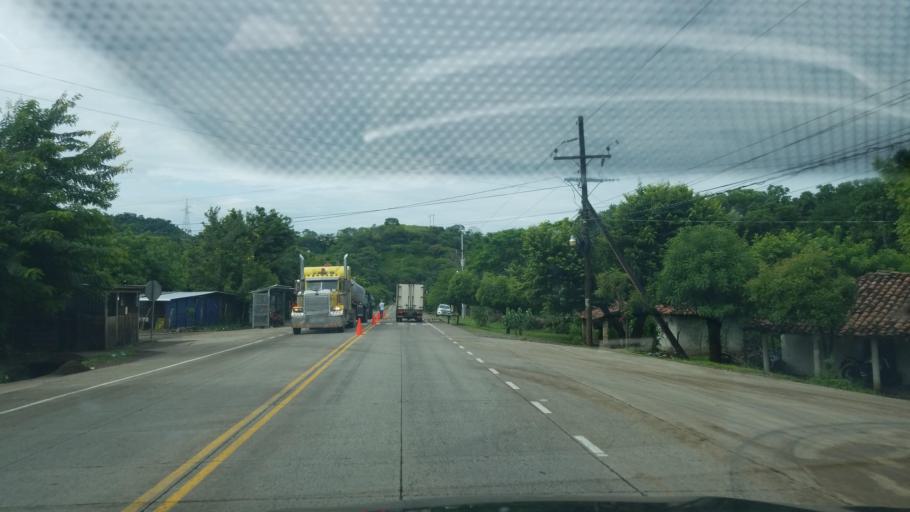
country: HN
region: Choluteca
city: Pespire
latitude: 13.6370
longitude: -87.3692
